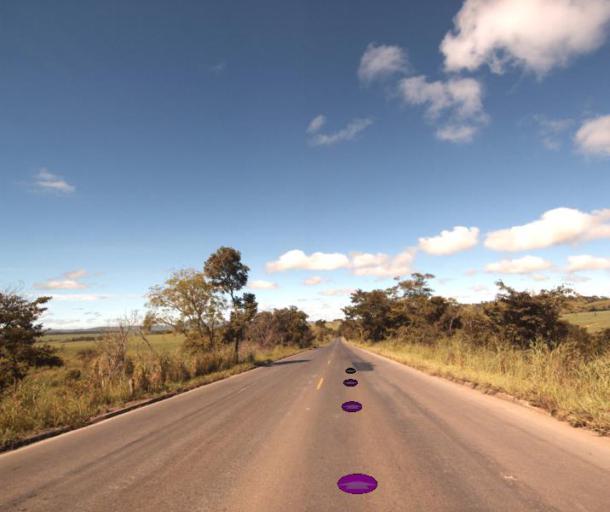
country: BR
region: Goias
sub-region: Itapaci
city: Itapaci
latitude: -15.0780
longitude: -49.4614
